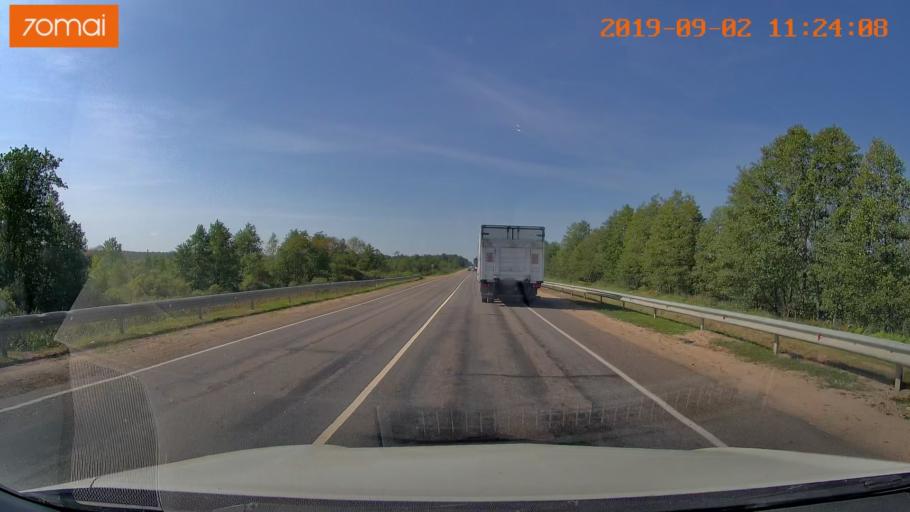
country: RU
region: Smolensk
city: Roslavl'
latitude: 54.0125
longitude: 32.9804
